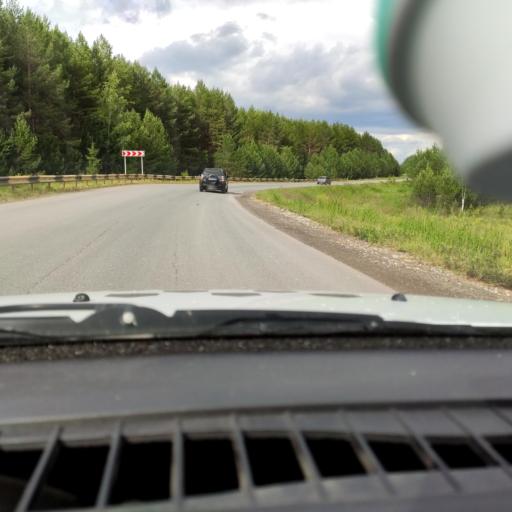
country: RU
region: Perm
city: Orda
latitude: 57.1491
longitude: 56.7593
